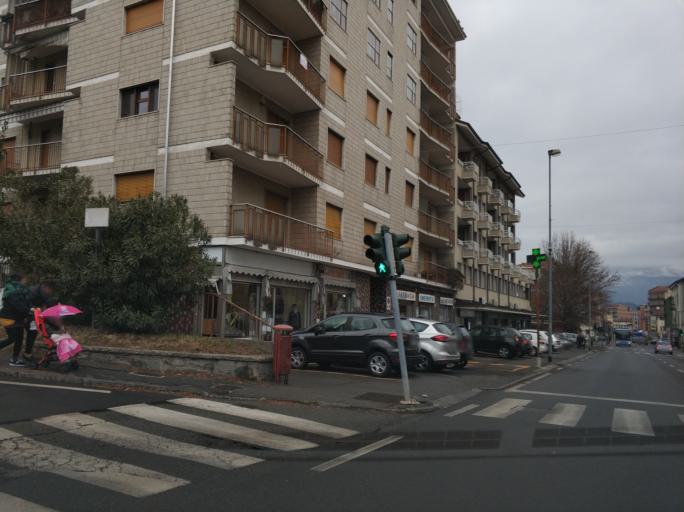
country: IT
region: Piedmont
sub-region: Provincia di Torino
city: Ivrea
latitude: 45.4524
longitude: 7.8787
